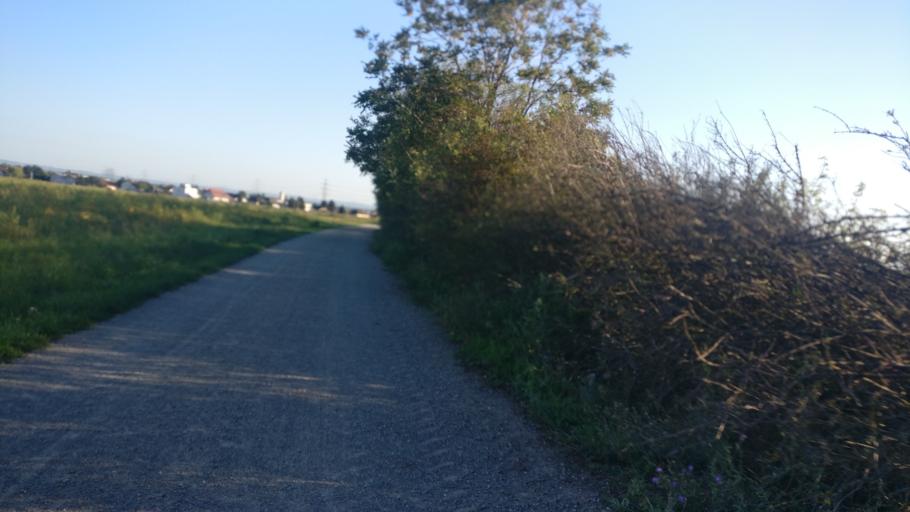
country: AT
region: Lower Austria
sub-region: Politischer Bezirk Wien-Umgebung
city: Lanzendorf
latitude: 48.1150
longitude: 16.4349
